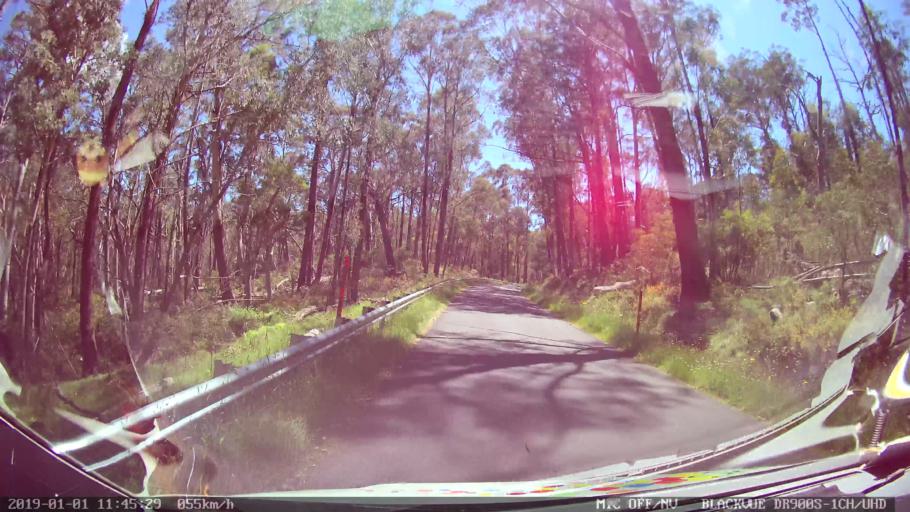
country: AU
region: New South Wales
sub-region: Snowy River
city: Jindabyne
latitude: -35.8963
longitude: 148.3958
